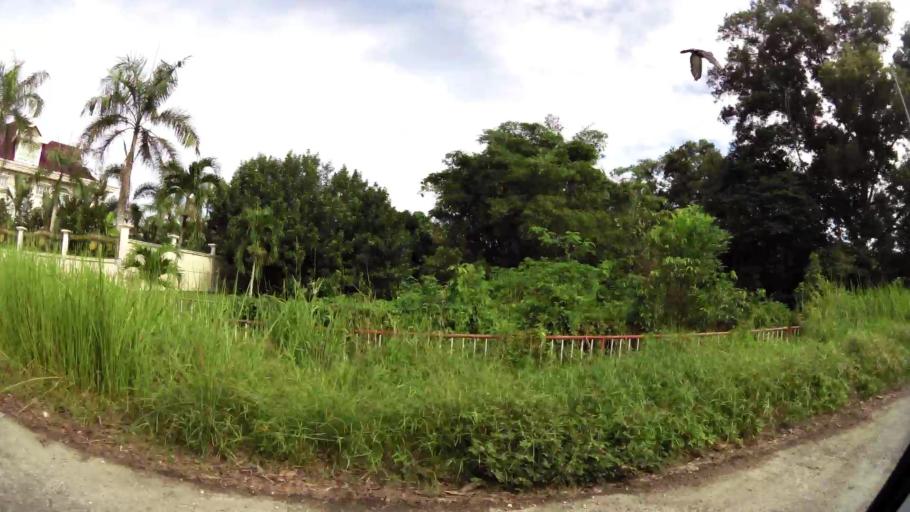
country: BN
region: Brunei and Muara
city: Bandar Seri Begawan
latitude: 4.8966
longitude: 114.8922
